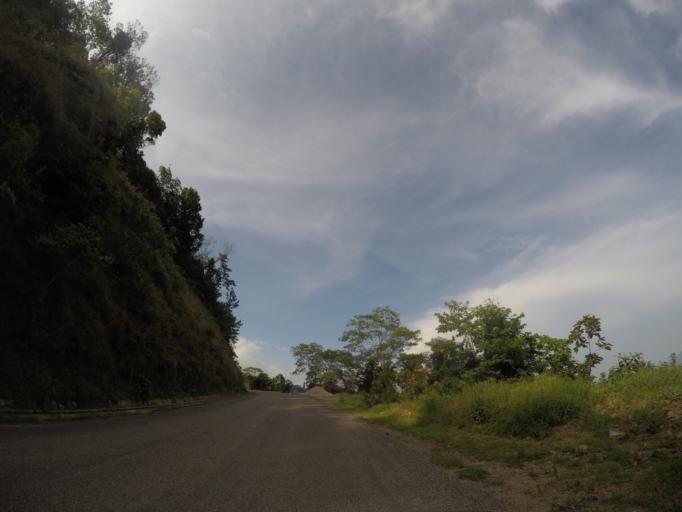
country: MX
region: Oaxaca
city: Pluma Hidalgo
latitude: 15.9357
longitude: -96.4321
